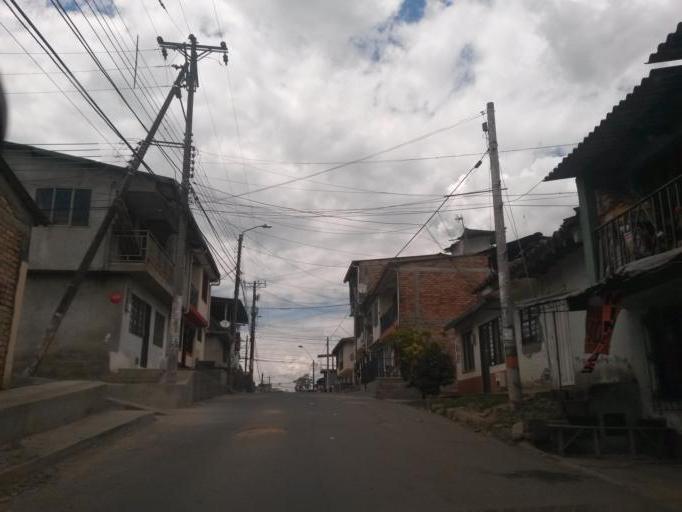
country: CO
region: Cauca
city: Popayan
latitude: 2.4479
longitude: -76.6270
